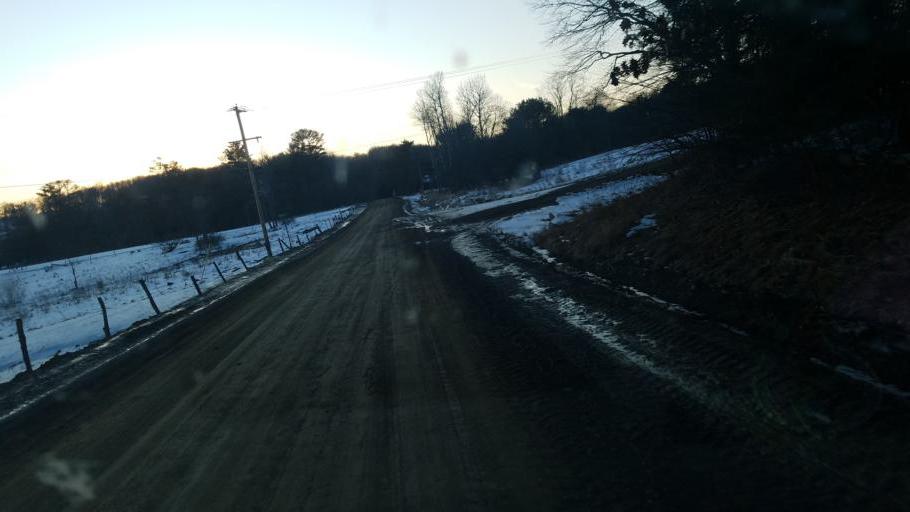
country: US
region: Pennsylvania
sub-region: Tioga County
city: Westfield
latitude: 42.0129
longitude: -77.6801
